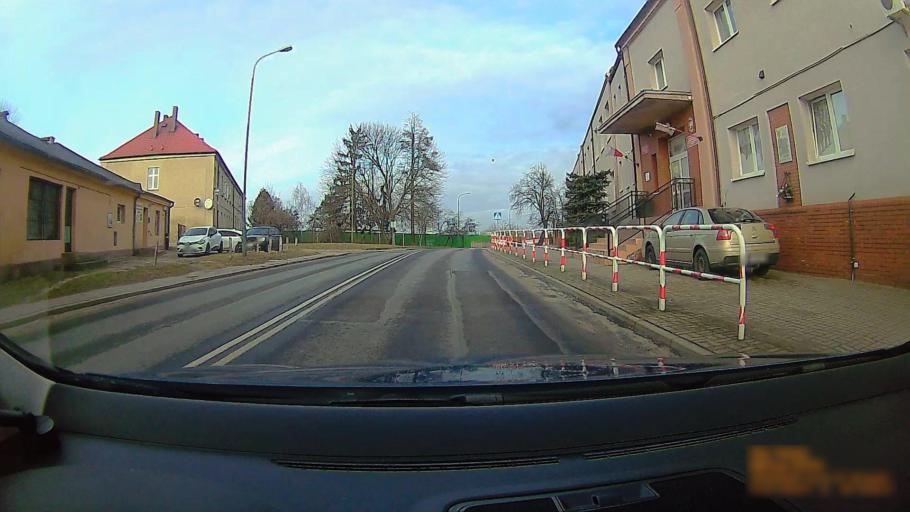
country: PL
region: Greater Poland Voivodeship
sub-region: Konin
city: Konin
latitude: 52.2028
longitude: 18.2485
